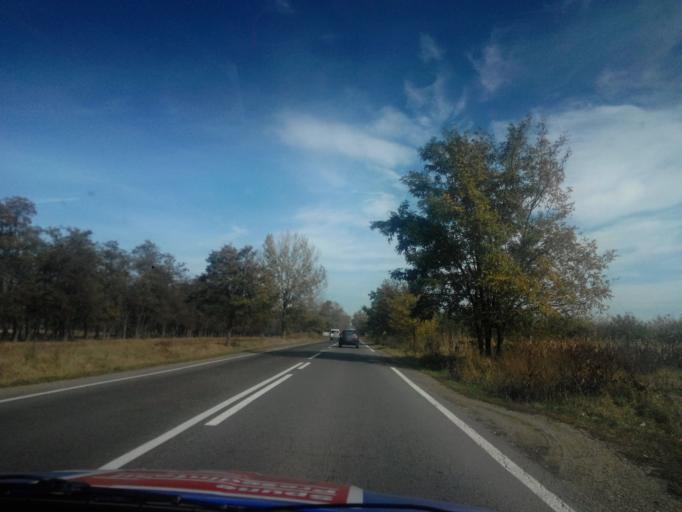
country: RO
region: Bacau
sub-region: Comuna Magura
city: Magura
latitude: 46.5498
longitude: 26.8704
